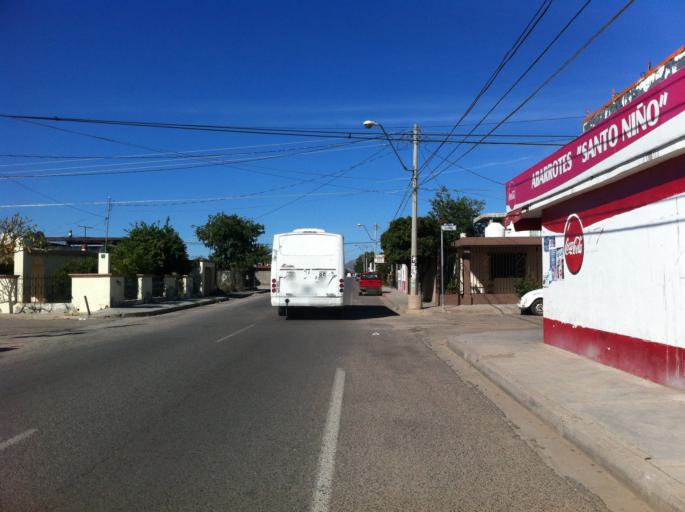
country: MX
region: Sonora
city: Hermosillo
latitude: 29.1111
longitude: -111.0114
